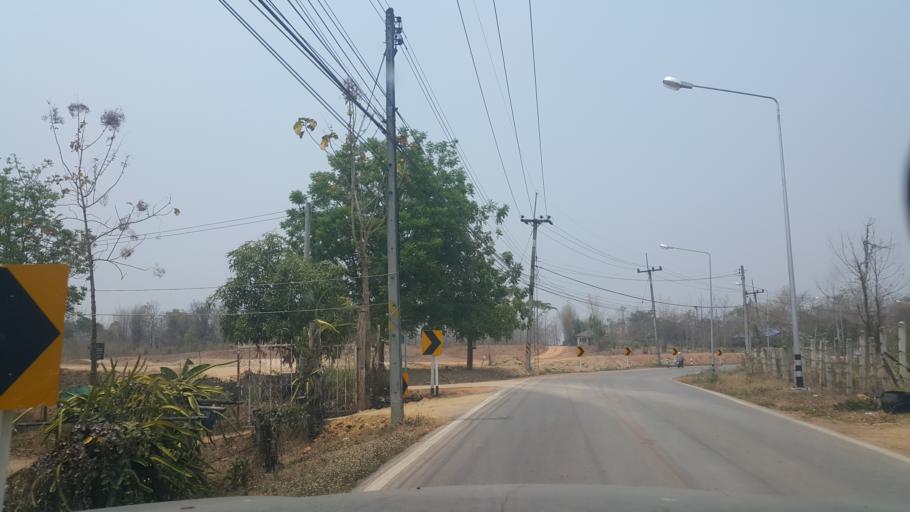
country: TH
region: Lampang
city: Soem Ngam
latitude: 18.0682
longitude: 99.2371
